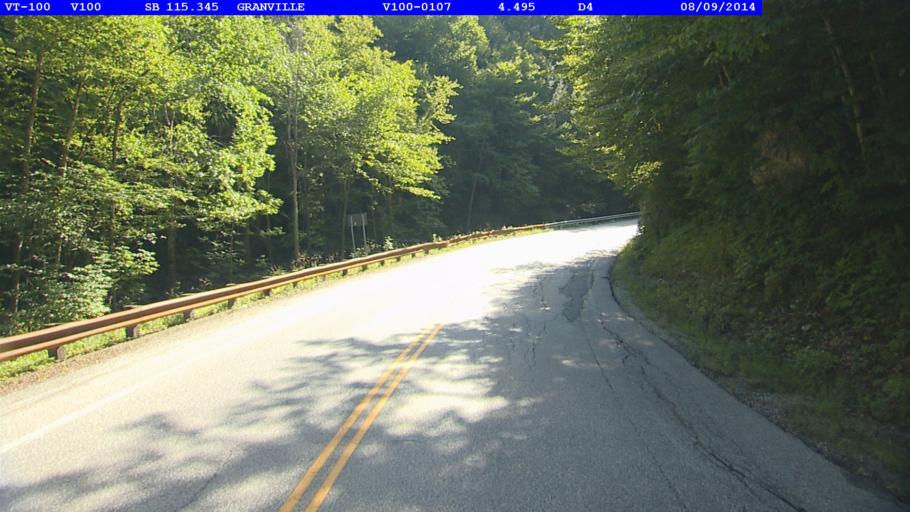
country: US
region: Vermont
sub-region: Orange County
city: Randolph
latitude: 44.0036
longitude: -72.8496
